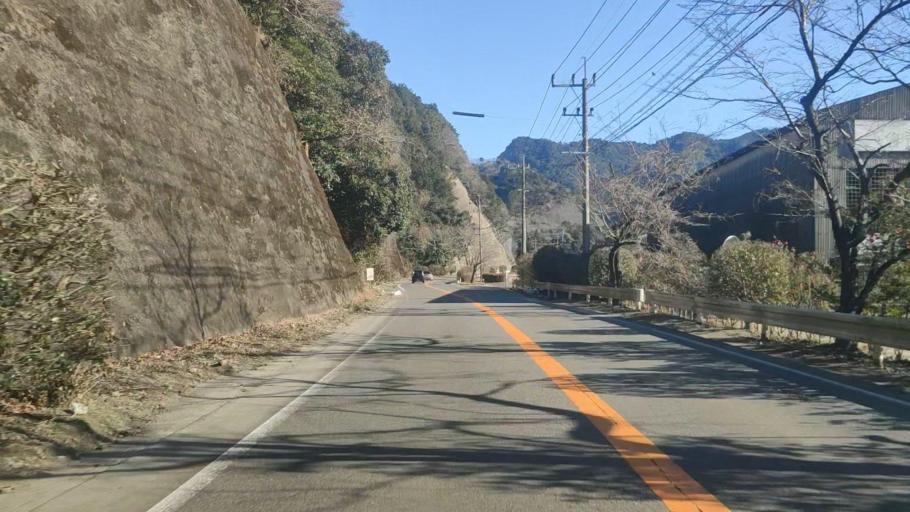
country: JP
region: Miyazaki
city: Nobeoka
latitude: 32.6224
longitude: 131.7085
